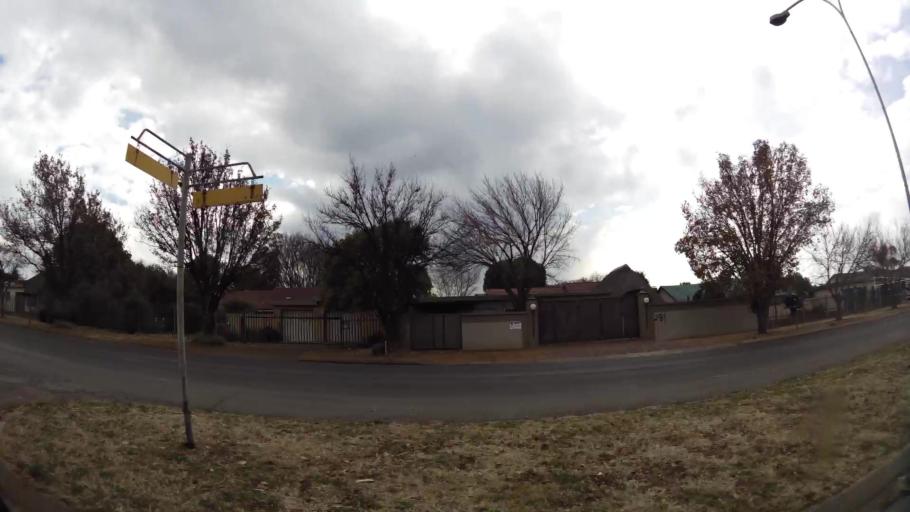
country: ZA
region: Gauteng
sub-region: Sedibeng District Municipality
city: Vanderbijlpark
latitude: -26.7303
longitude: 27.8563
